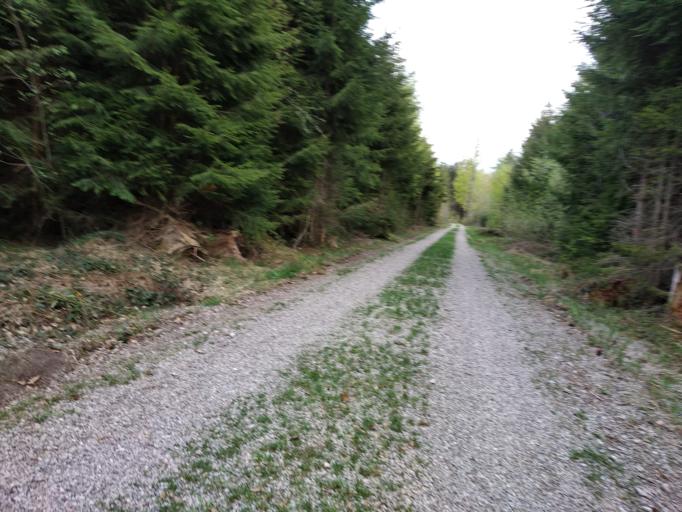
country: DE
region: Bavaria
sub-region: Swabia
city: Woringen
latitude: 47.9293
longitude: 10.1915
